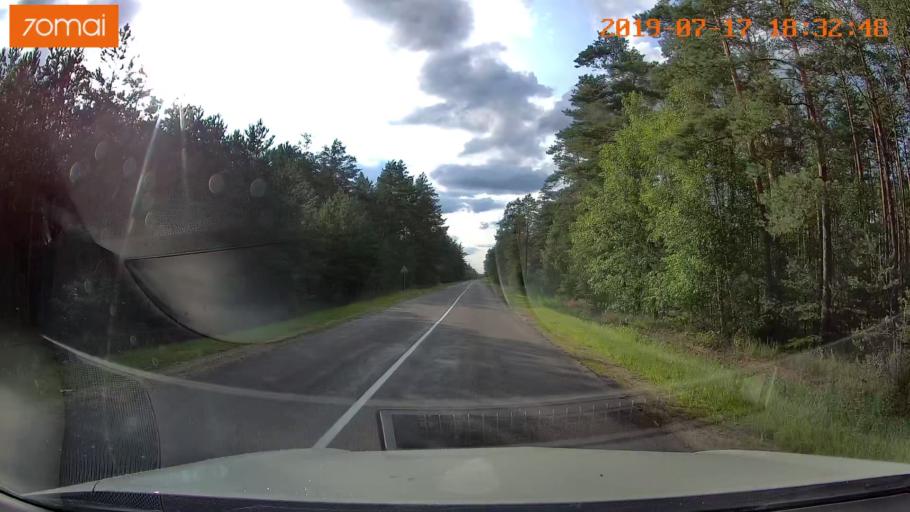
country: BY
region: Mogilev
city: Asipovichy
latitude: 53.2746
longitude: 28.6739
